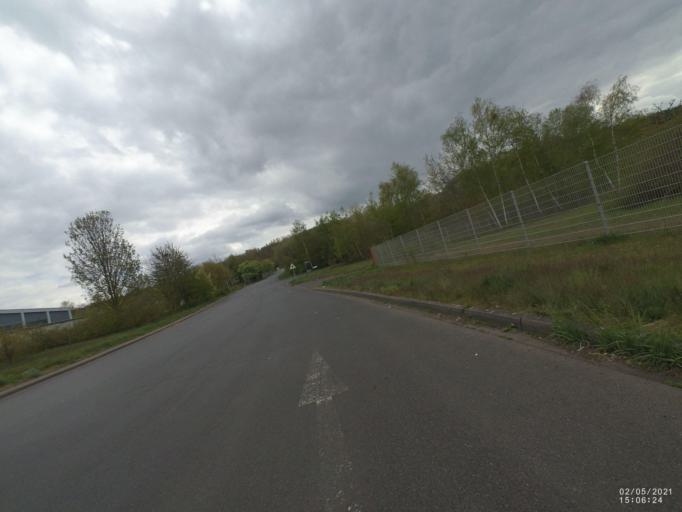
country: DE
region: Rheinland-Pfalz
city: Saffig
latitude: 50.3551
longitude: 7.4288
